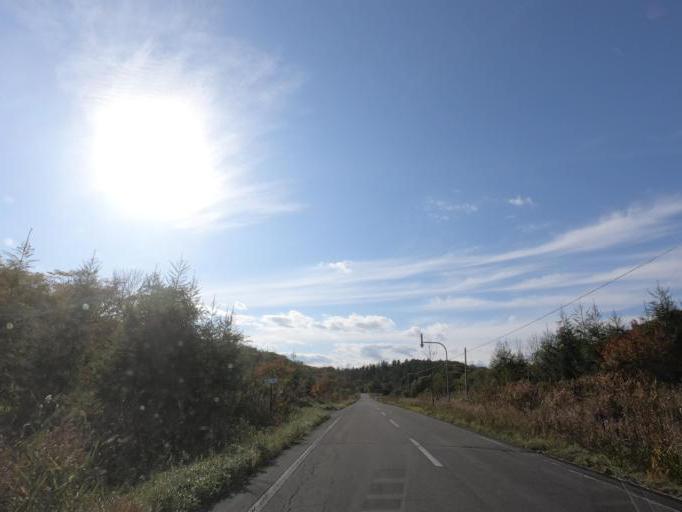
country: JP
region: Hokkaido
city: Obihiro
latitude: 42.6170
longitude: 143.4016
